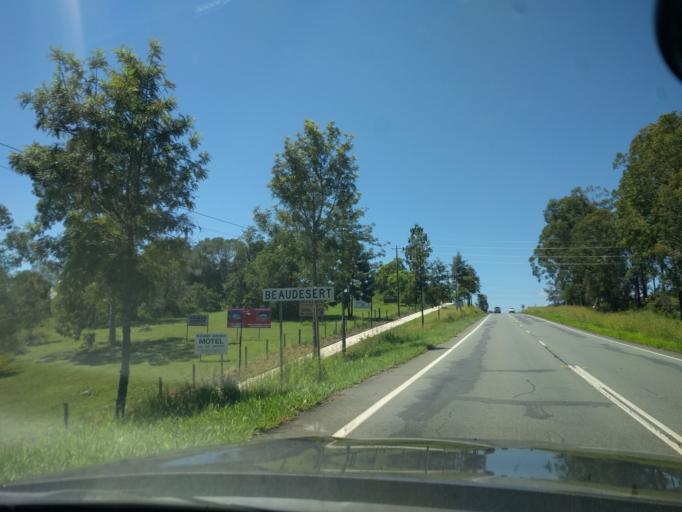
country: AU
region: Queensland
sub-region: Logan
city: Cedar Vale
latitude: -27.9642
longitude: 152.9957
